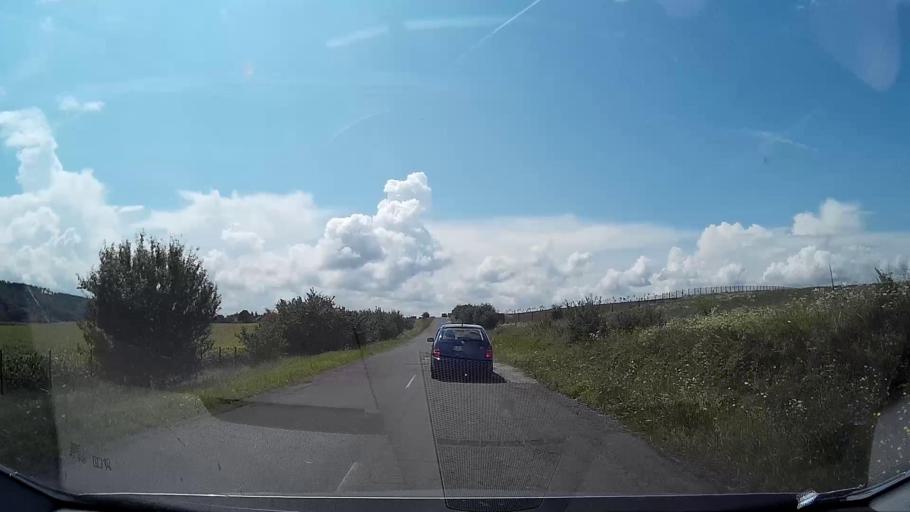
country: SK
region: Banskobystricky
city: Fil'akovo
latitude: 48.3323
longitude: 19.8192
